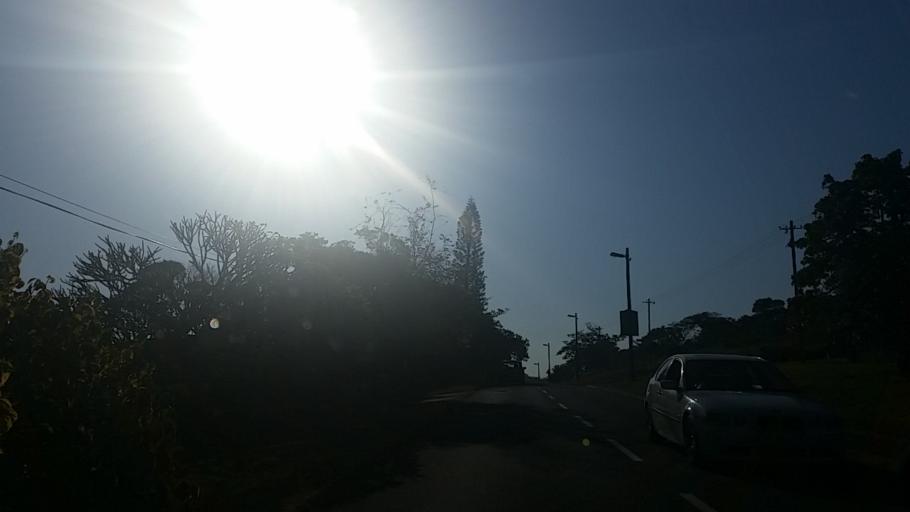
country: ZA
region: KwaZulu-Natal
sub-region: eThekwini Metropolitan Municipality
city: Berea
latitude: -29.8512
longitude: 30.9078
